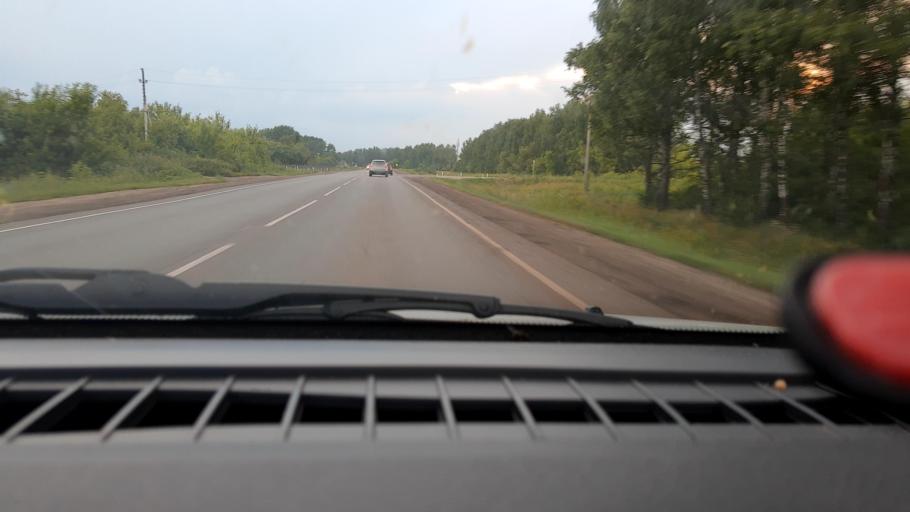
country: RU
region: Nizjnij Novgorod
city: Arzamas
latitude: 55.2931
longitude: 43.9405
